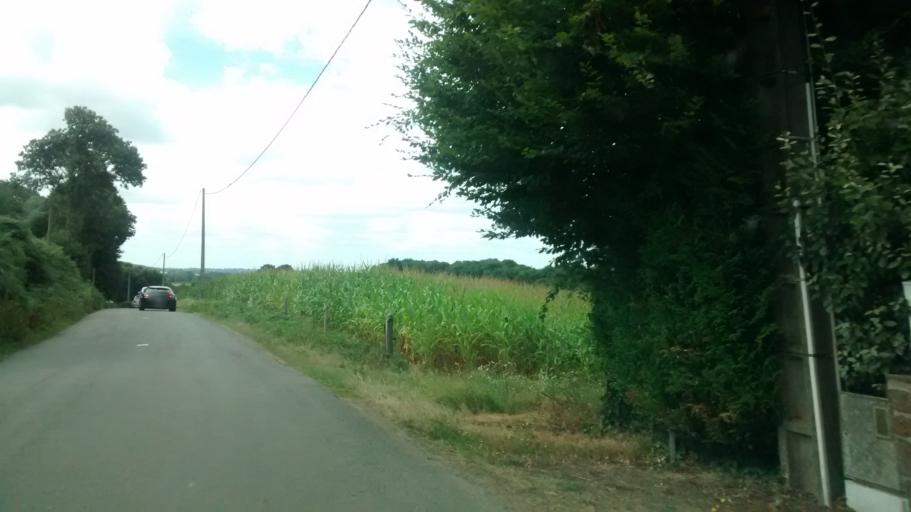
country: FR
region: Brittany
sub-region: Departement d'Ille-et-Vilaine
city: Hede-Bazouges
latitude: 48.2922
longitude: -1.8307
